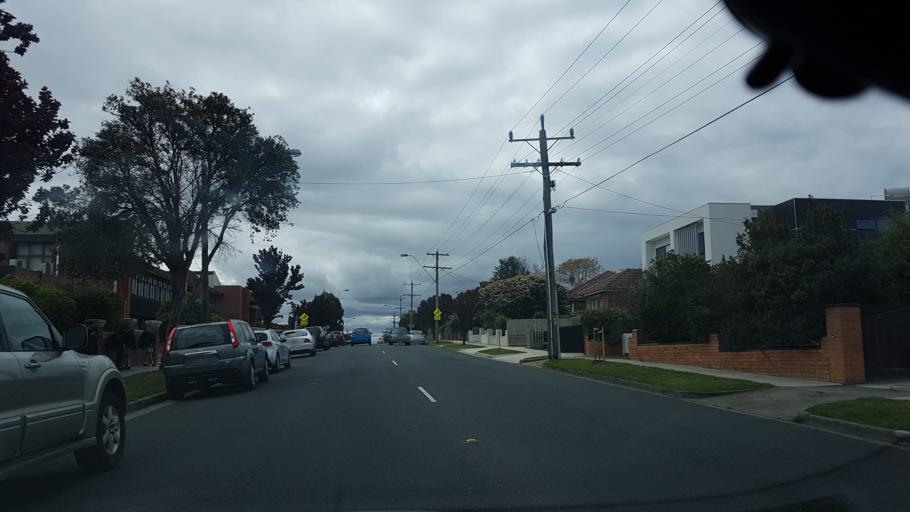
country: AU
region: Victoria
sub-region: Glen Eira
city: Bentleigh
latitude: -37.9259
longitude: 145.0403
